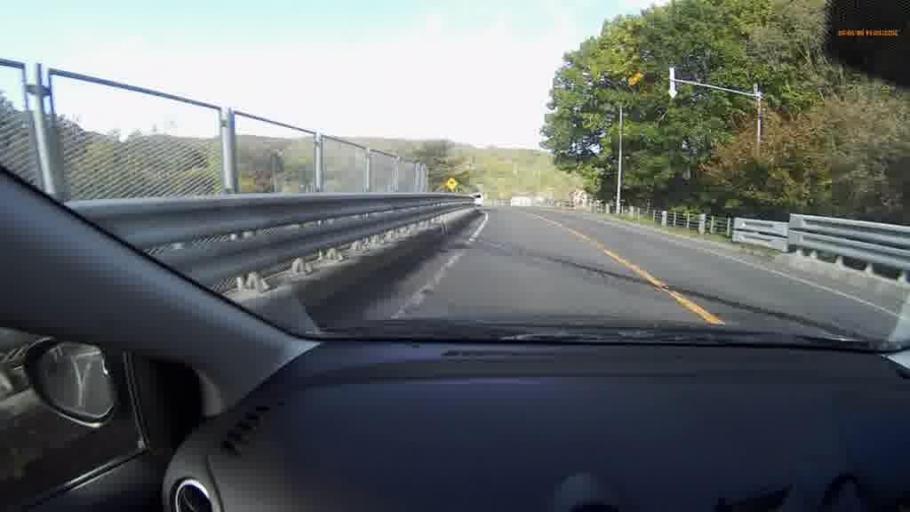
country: JP
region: Hokkaido
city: Kushiro
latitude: 42.9971
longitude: 144.4817
